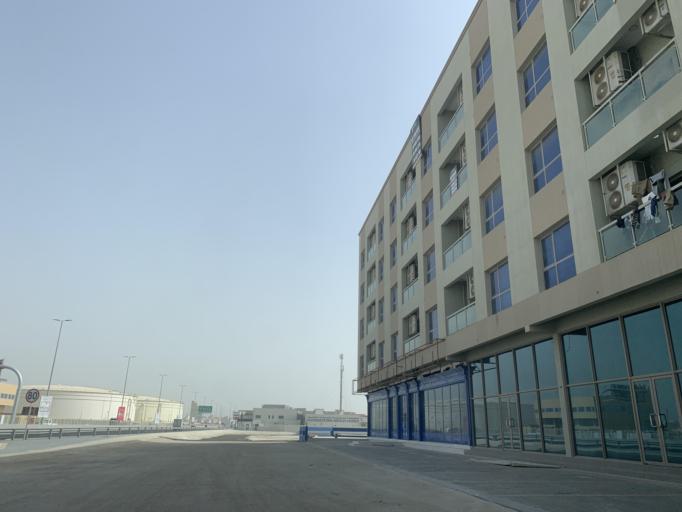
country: BH
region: Northern
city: Madinat `Isa
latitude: 26.1891
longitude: 50.5178
